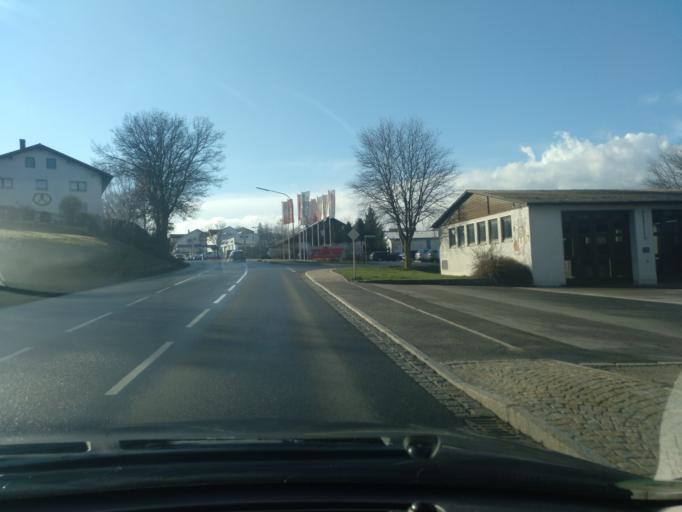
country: DE
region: Bavaria
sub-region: Upper Palatinate
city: Zandt
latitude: 49.1560
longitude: 12.7299
